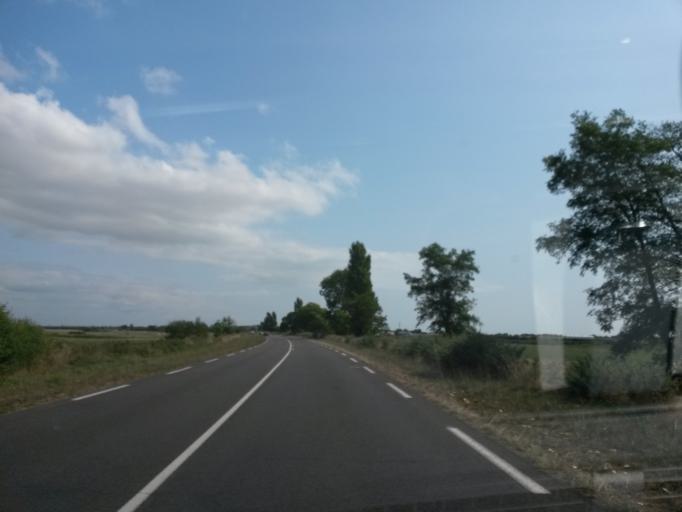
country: FR
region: Pays de la Loire
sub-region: Departement de la Vendee
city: La Tranche-sur-Mer
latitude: 46.3572
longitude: -1.4434
